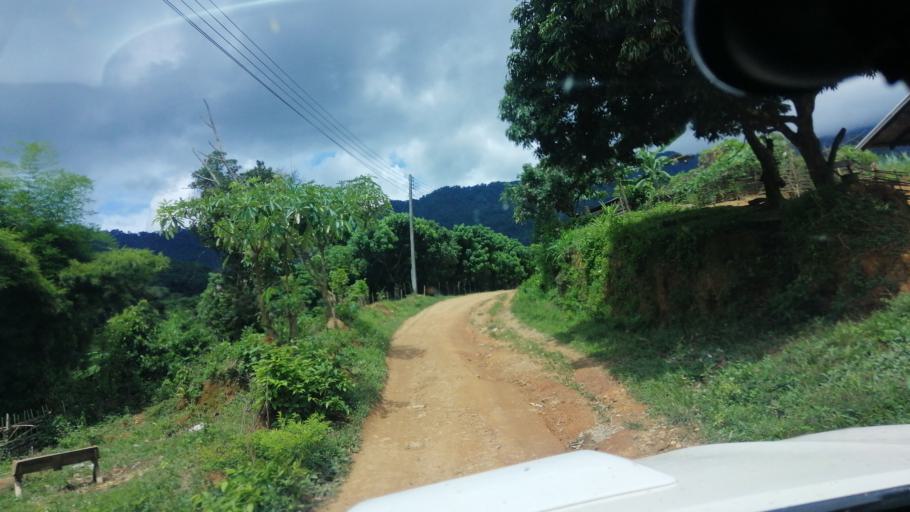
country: TH
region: Phayao
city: Phu Sang
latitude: 19.7450
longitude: 100.4299
